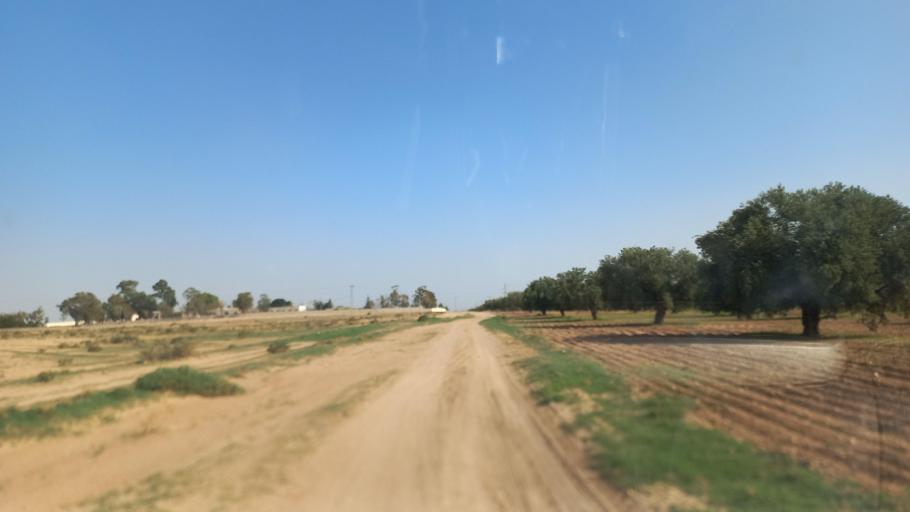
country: TN
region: Al Qasrayn
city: Kasserine
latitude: 35.2982
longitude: 9.0294
